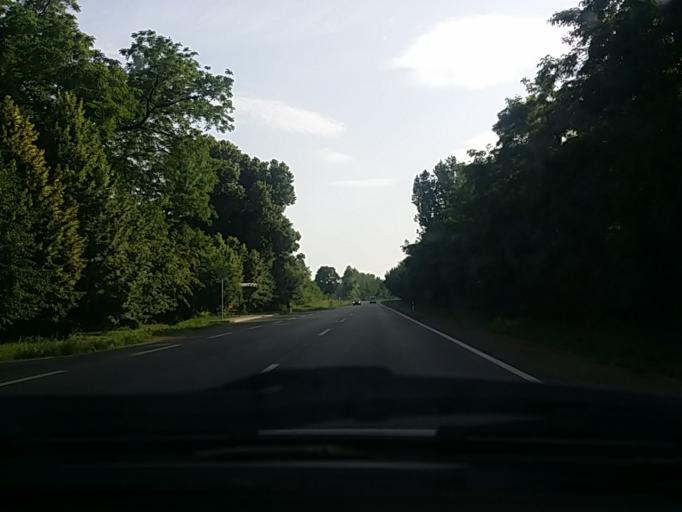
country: HU
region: Jasz-Nagykun-Szolnok
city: Jaszbereny
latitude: 47.4785
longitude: 19.8702
